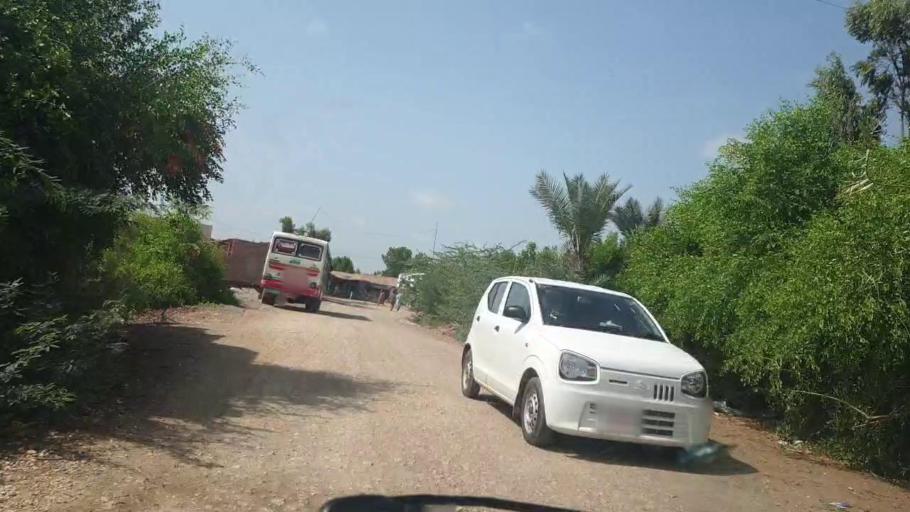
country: PK
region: Sindh
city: Berani
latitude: 25.7403
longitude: 68.9542
